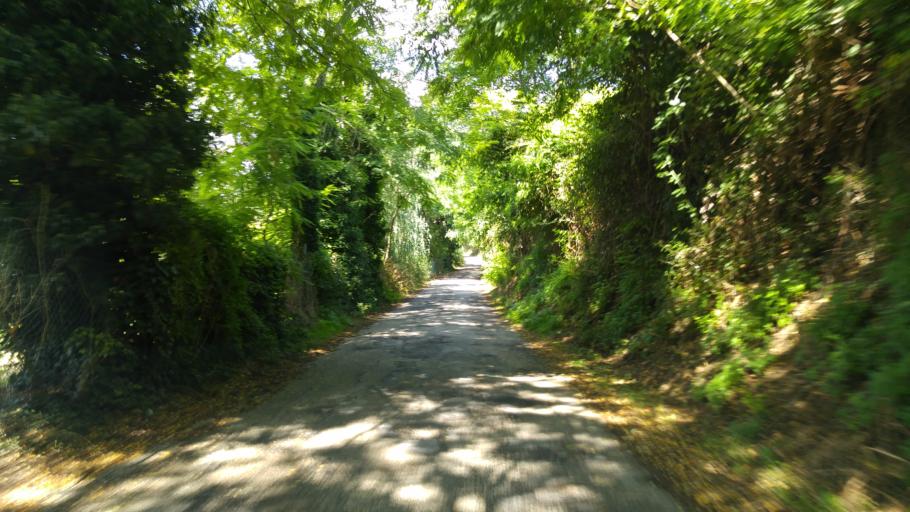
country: IT
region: The Marches
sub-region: Provincia di Pesaro e Urbino
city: Centinarola
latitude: 43.8158
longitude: 12.9727
